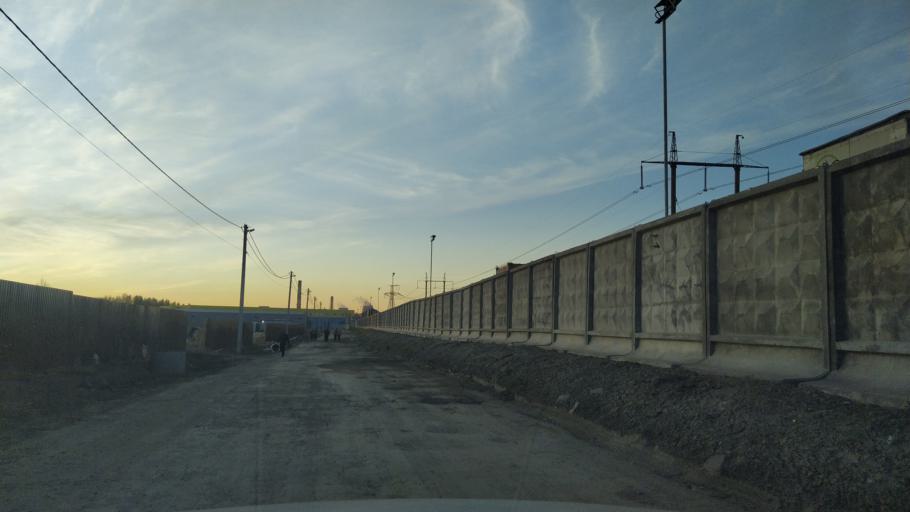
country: RU
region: St.-Petersburg
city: Obukhovo
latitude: 59.8027
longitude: 30.4602
